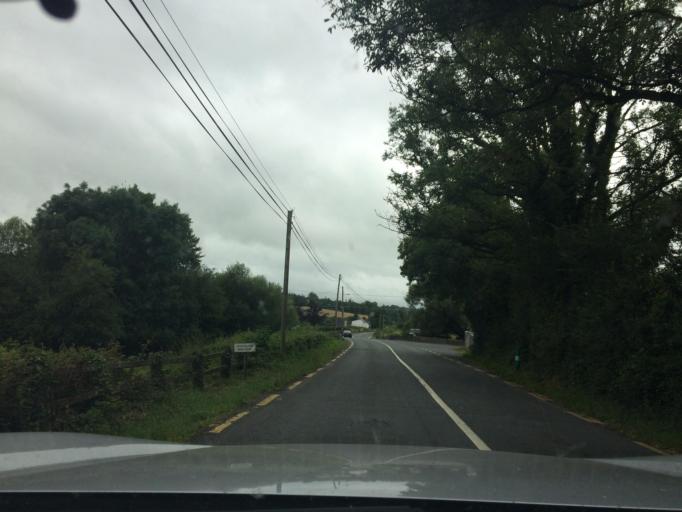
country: IE
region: Munster
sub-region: South Tipperary
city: Cluain Meala
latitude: 52.3174
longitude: -7.7759
